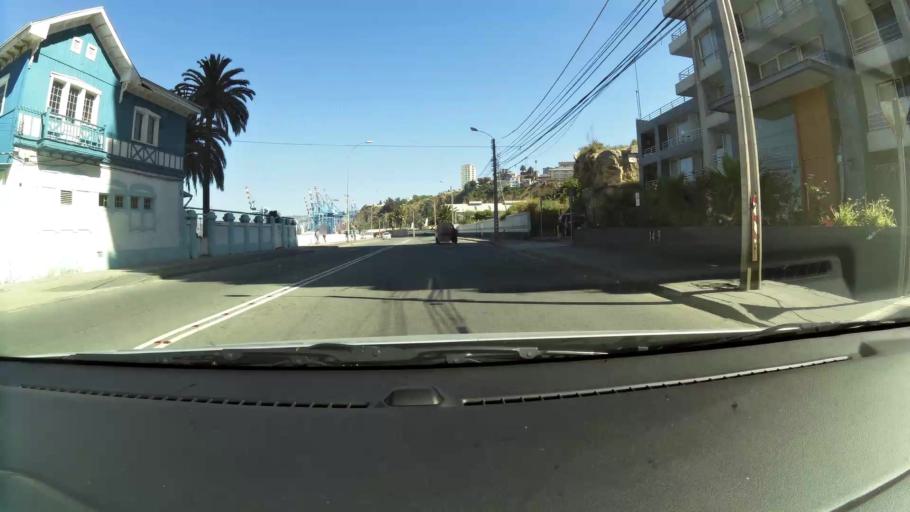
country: CL
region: Valparaiso
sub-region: Provincia de Valparaiso
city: Valparaiso
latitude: -33.0231
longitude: -71.6328
